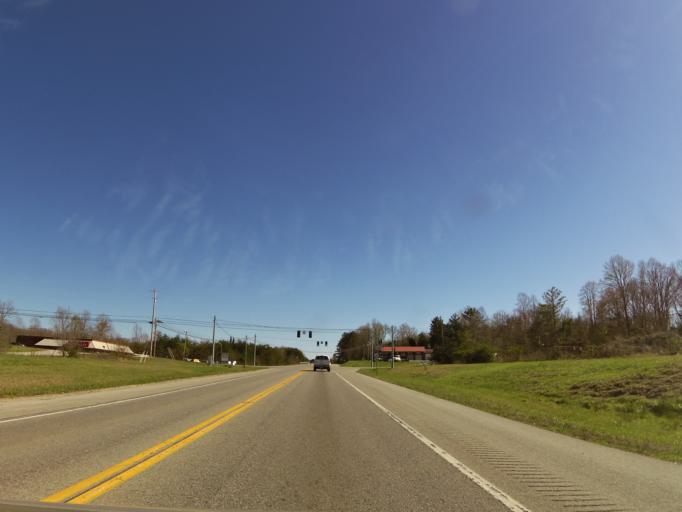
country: US
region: Kentucky
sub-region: McCreary County
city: Stearns
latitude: 36.6949
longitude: -84.4564
